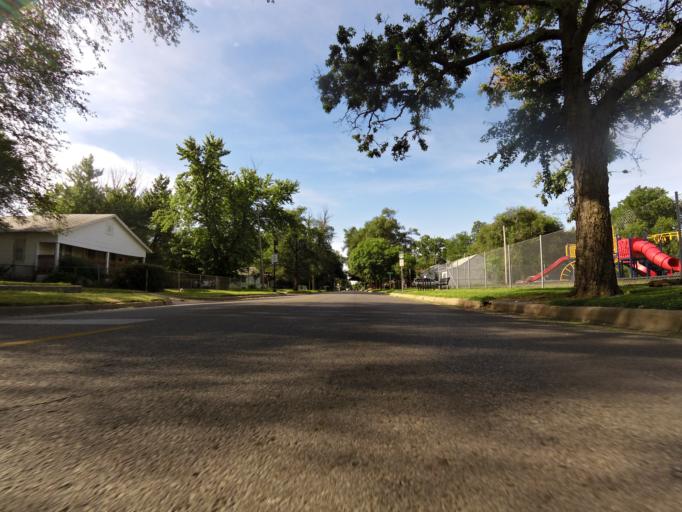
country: US
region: Kansas
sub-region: Sedgwick County
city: Wichita
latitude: 37.7032
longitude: -97.3082
